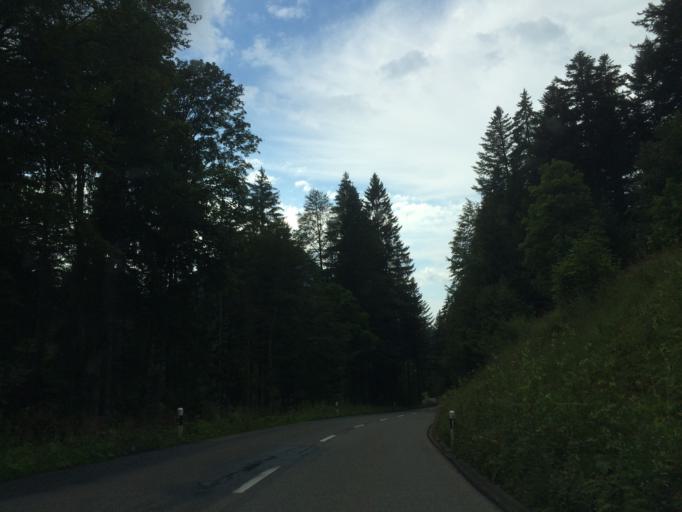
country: CH
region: Appenzell Ausserrhoden
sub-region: Bezirk Hinterland
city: Urnasch
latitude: 47.2467
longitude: 9.2813
